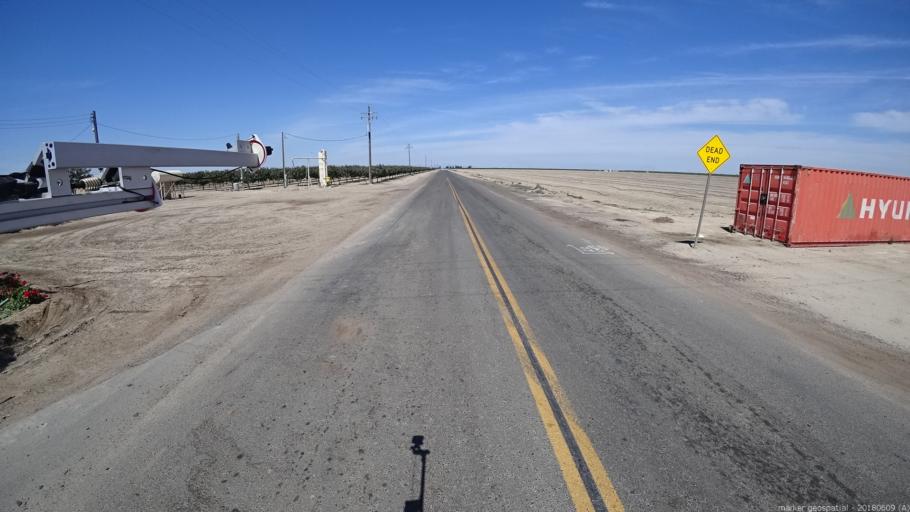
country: US
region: California
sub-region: Fresno County
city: Firebaugh
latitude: 36.9525
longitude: -120.3827
